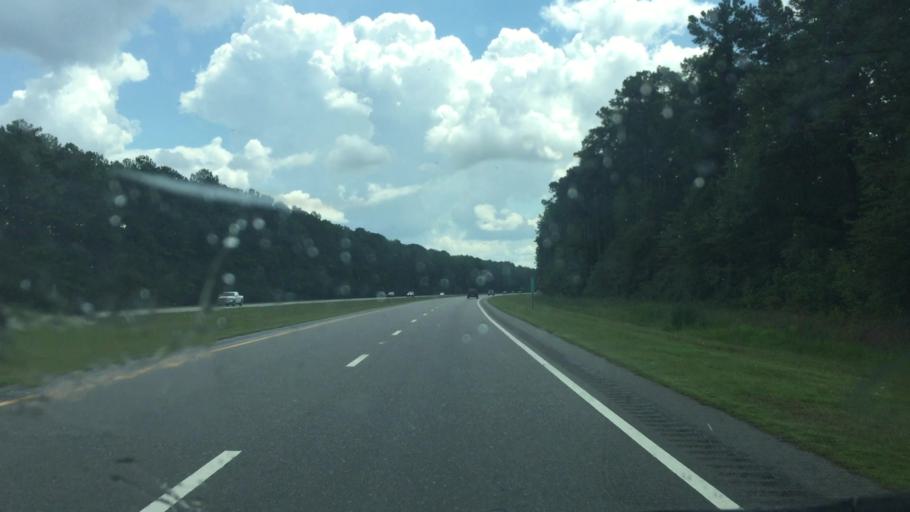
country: US
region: North Carolina
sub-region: Columbus County
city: Chadbourn
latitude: 34.3788
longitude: -78.8517
